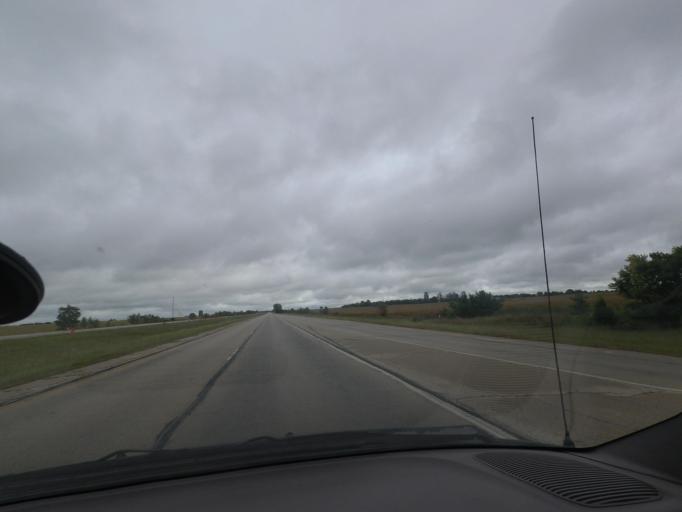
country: US
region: Illinois
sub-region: Piatt County
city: Cerro Gordo
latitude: 40.0167
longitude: -88.7419
